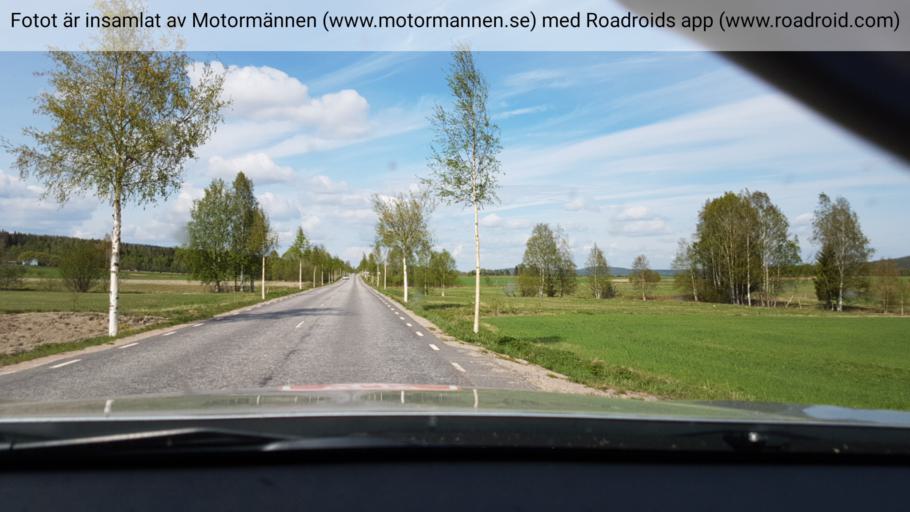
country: SE
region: Vaesterbotten
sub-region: Vannas Kommun
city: Vannasby
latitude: 63.8536
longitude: 19.9067
